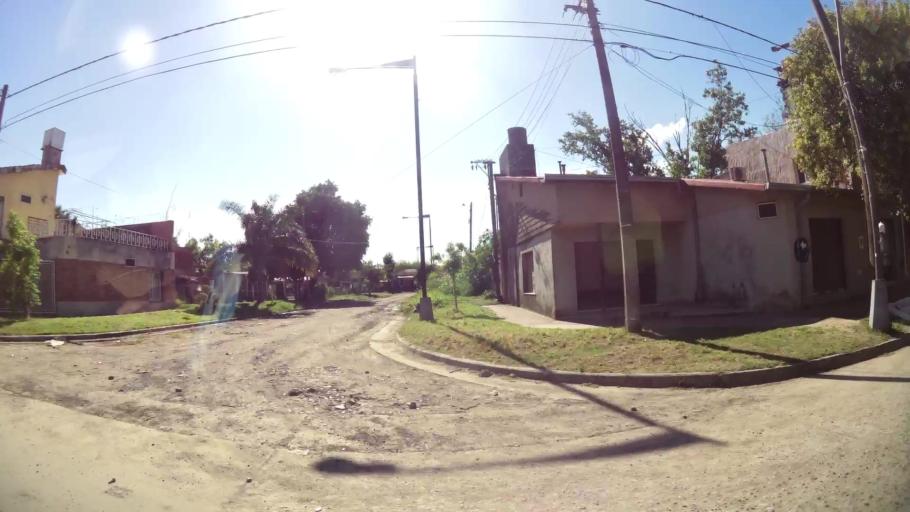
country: AR
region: Santa Fe
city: Santa Fe de la Vera Cruz
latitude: -31.6258
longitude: -60.6944
